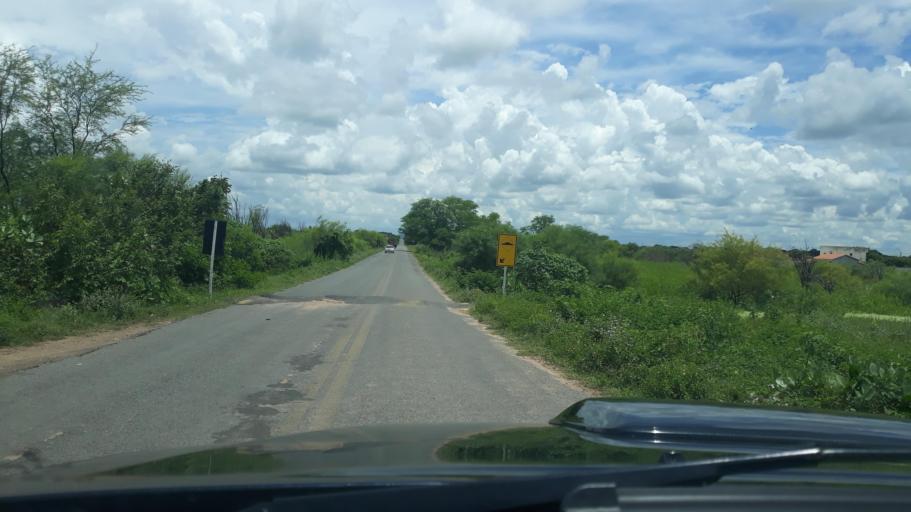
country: BR
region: Bahia
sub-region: Guanambi
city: Guanambi
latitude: -13.9121
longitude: -42.8434
